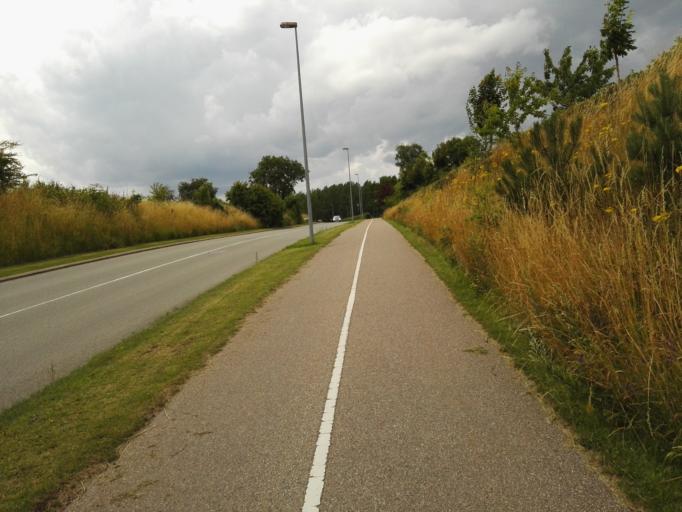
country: DK
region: Capital Region
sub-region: Egedal Kommune
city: Stenlose
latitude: 55.7864
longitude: 12.1796
